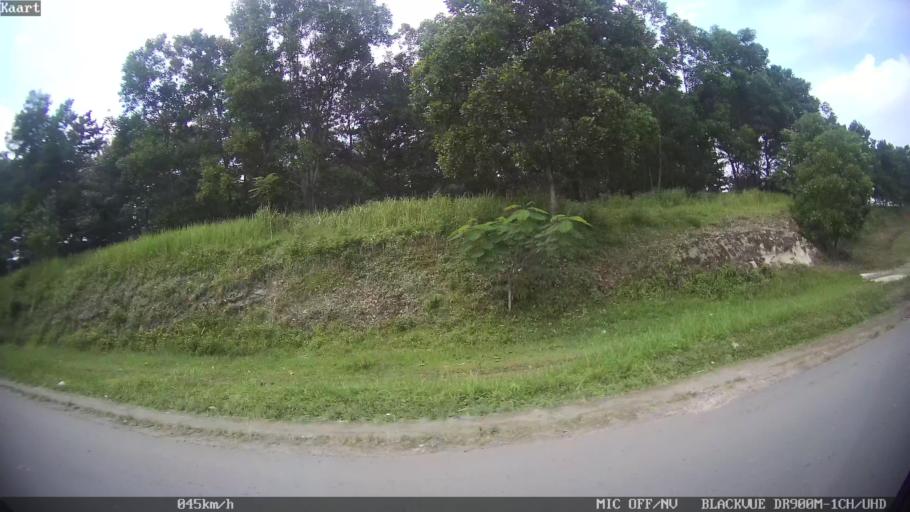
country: ID
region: Lampung
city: Kedaton
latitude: -5.3563
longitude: 105.3164
